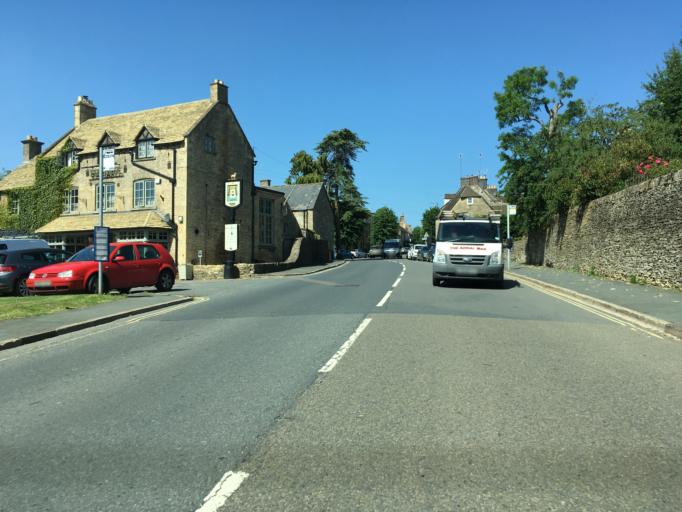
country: GB
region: England
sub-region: Gloucestershire
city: Stow on the Wold
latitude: 51.9287
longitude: -1.7177
